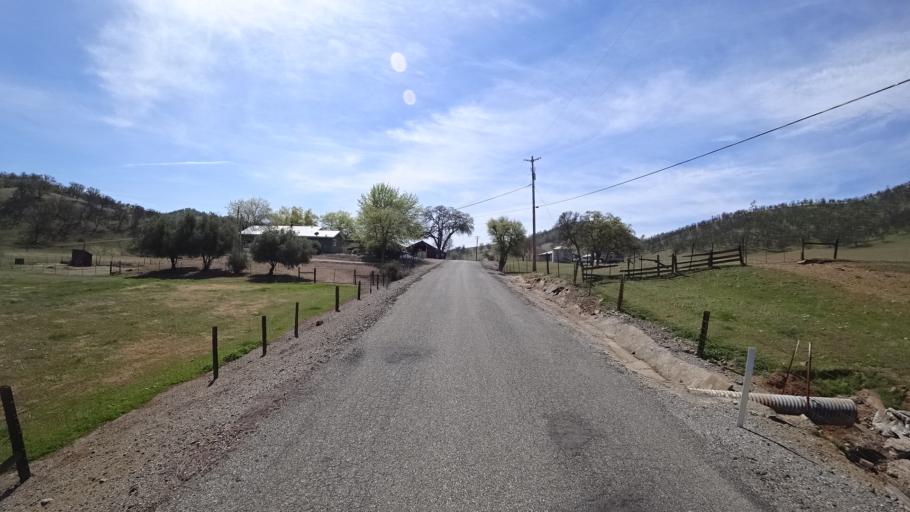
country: US
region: California
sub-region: Glenn County
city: Willows
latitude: 39.5197
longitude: -122.4569
